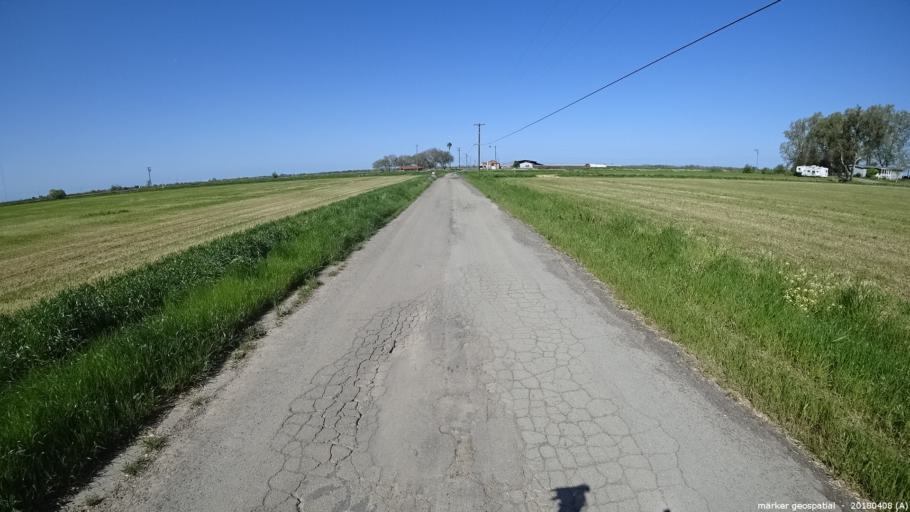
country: US
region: California
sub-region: Sacramento County
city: Walnut Grove
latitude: 38.3277
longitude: -121.4711
